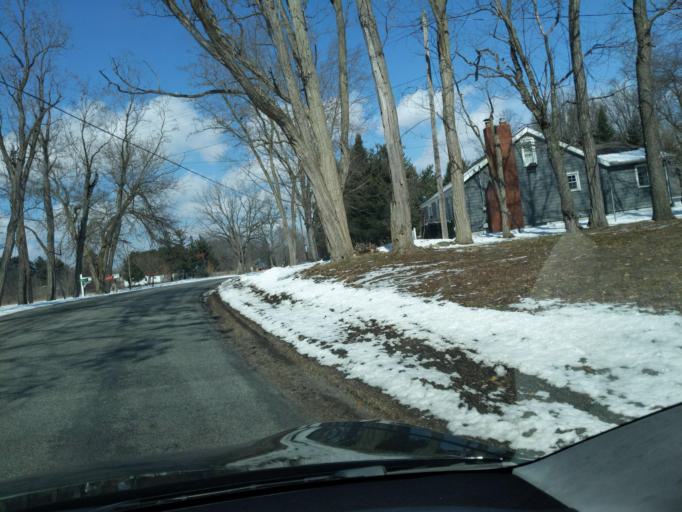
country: US
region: Michigan
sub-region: Ingham County
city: Mason
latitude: 42.6073
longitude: -84.4673
